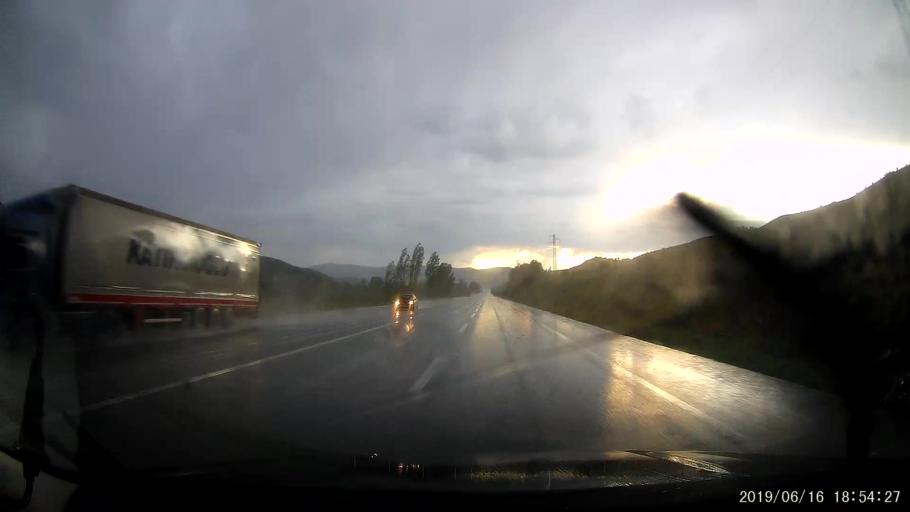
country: TR
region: Erzincan
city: Catalcam
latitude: 39.8970
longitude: 38.8535
